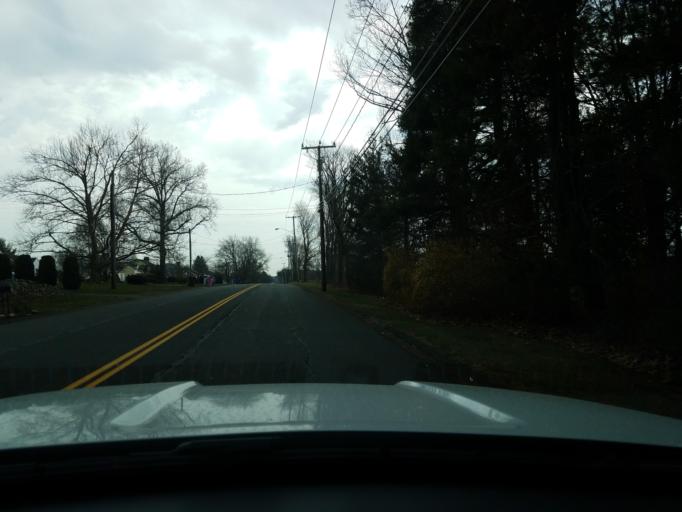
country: US
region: Connecticut
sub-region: Hartford County
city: Newington
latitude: 41.6843
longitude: -72.6914
